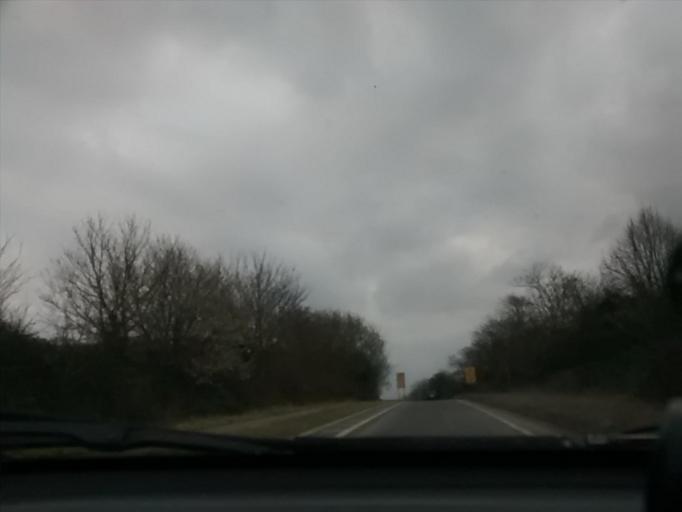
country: GB
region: England
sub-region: Cambridgeshire
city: Sawston
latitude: 52.1585
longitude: 0.1761
